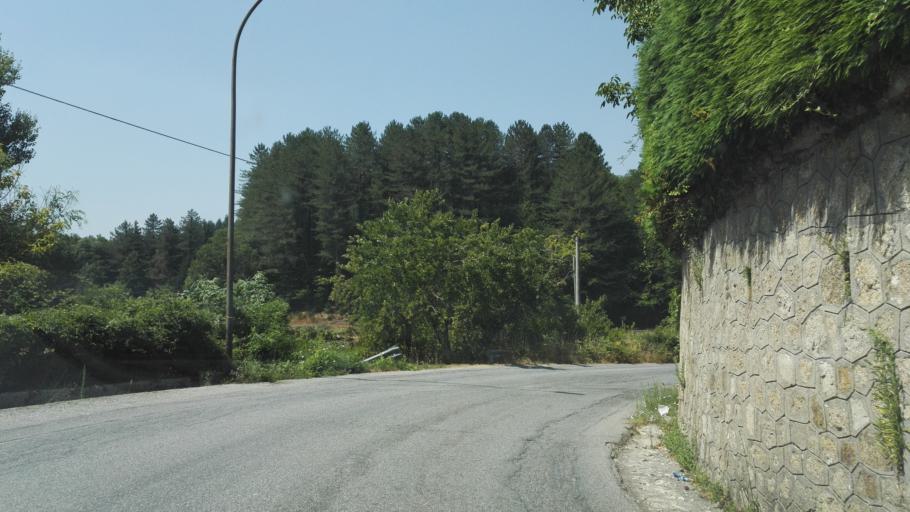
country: IT
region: Calabria
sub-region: Provincia di Vibo-Valentia
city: Mongiana
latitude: 38.5146
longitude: 16.3164
